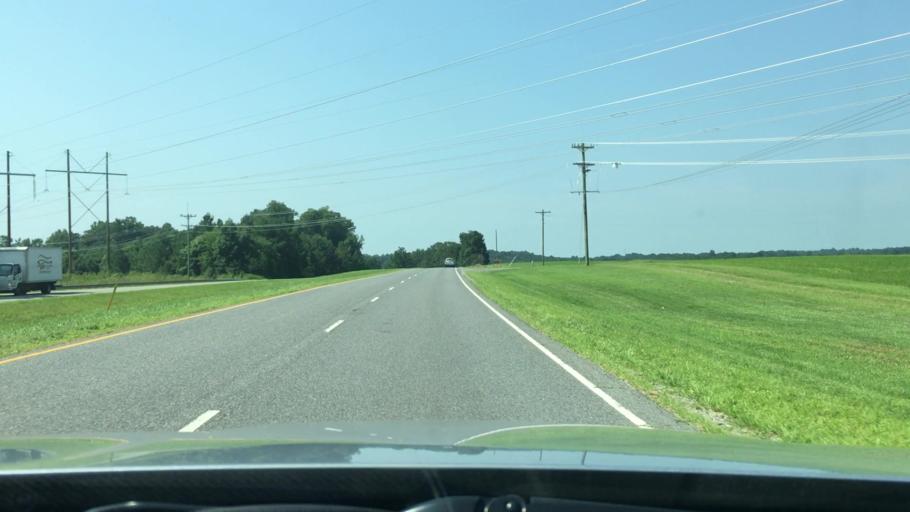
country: US
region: Virginia
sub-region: Caroline County
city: Bowling Green
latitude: 37.9779
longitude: -77.4234
